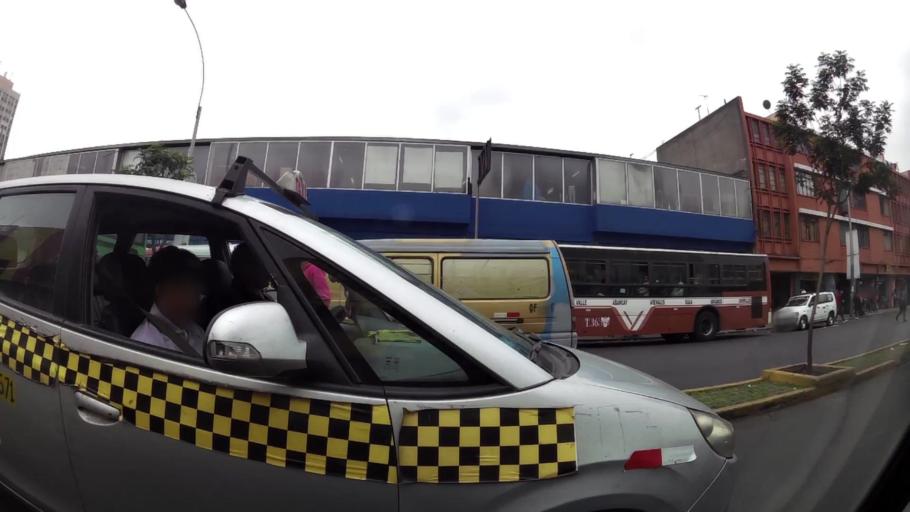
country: PE
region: Lima
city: Lima
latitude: -12.0574
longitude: -77.0301
